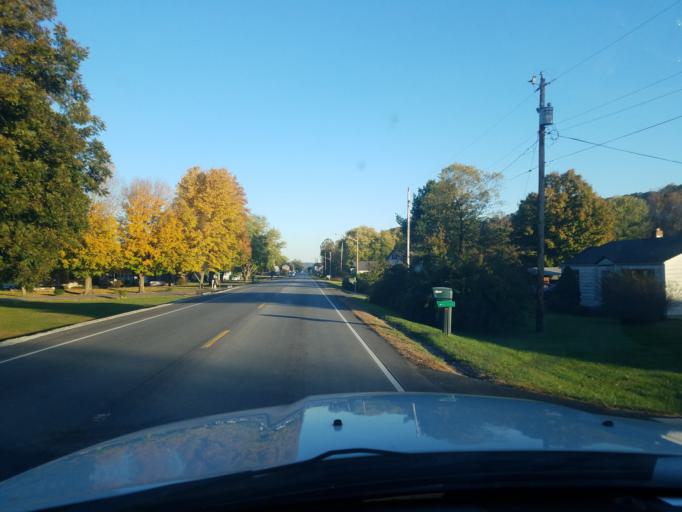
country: US
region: Indiana
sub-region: Washington County
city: New Pekin
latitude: 38.4689
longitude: -85.9530
